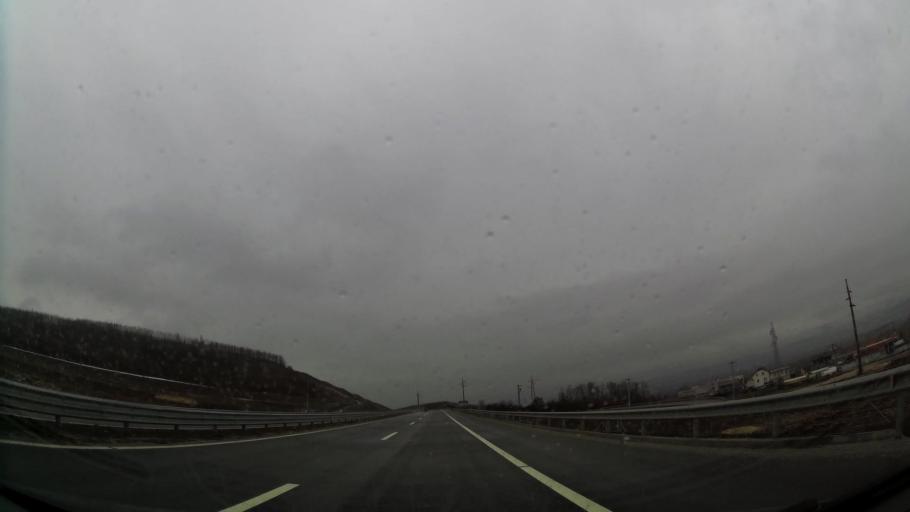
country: XK
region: Ferizaj
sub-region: Komuna e Ferizajt
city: Ferizaj
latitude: 42.3265
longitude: 21.2046
